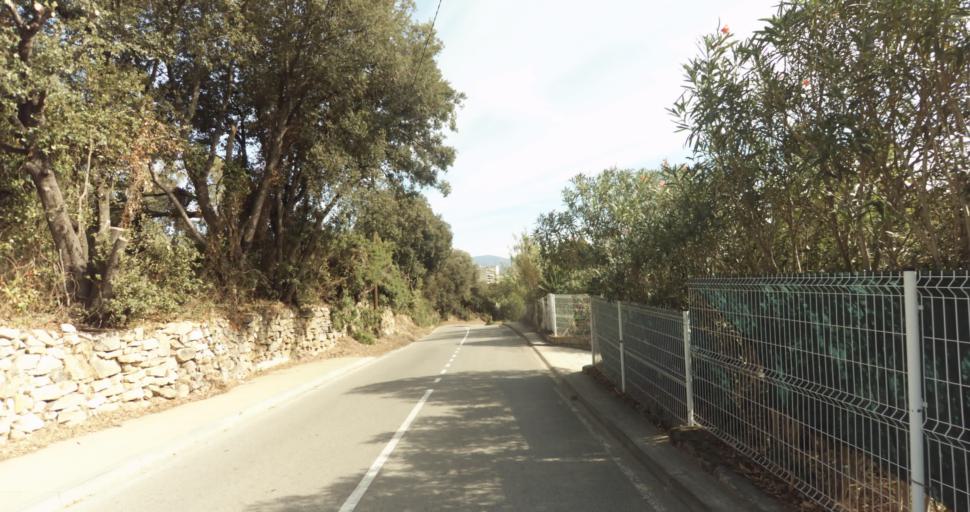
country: FR
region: Corsica
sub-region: Departement de la Corse-du-Sud
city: Ajaccio
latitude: 41.9382
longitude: 8.7353
